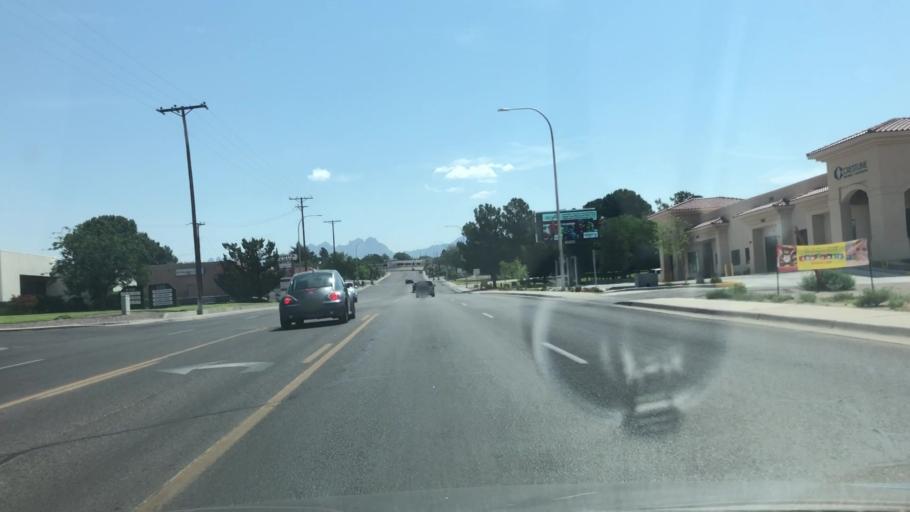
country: US
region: New Mexico
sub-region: Dona Ana County
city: University Park
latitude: 32.2993
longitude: -106.7395
